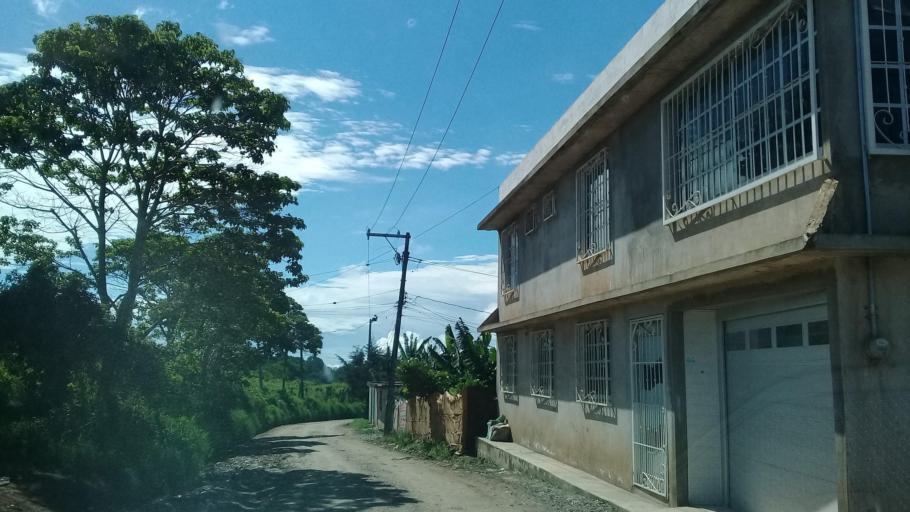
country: MX
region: Veracruz
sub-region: Jilotepec
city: El Pueblito (Garbanzal)
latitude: 19.5741
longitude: -96.9001
